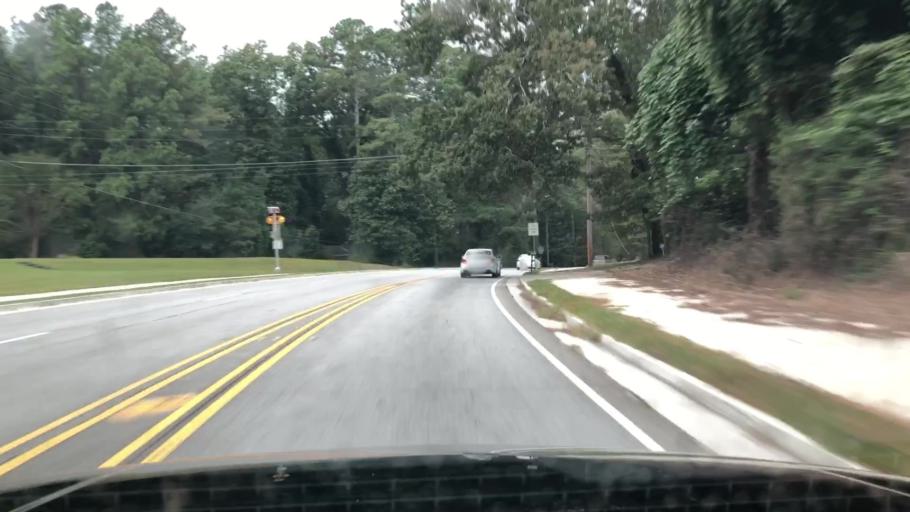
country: US
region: Georgia
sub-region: Fulton County
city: Union City
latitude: 33.7017
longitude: -84.5658
